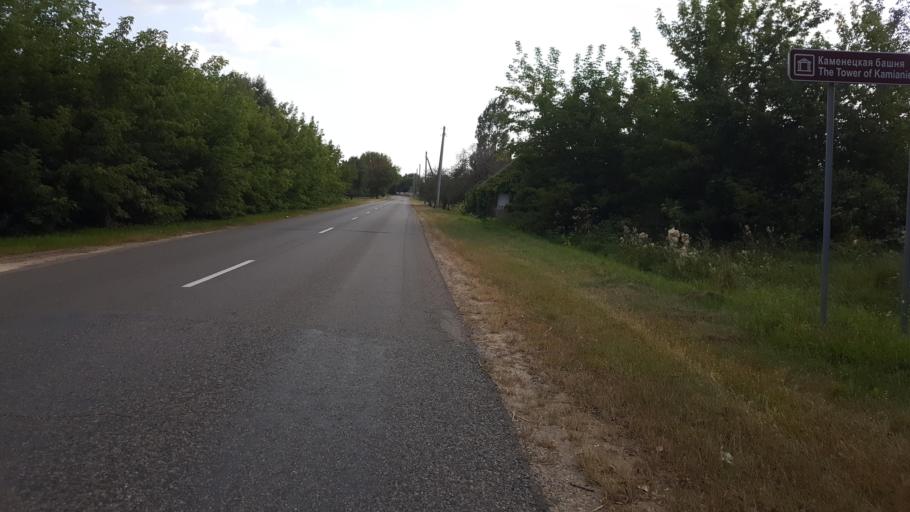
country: BY
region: Brest
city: Kamyanyets
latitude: 52.4079
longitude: 23.7892
